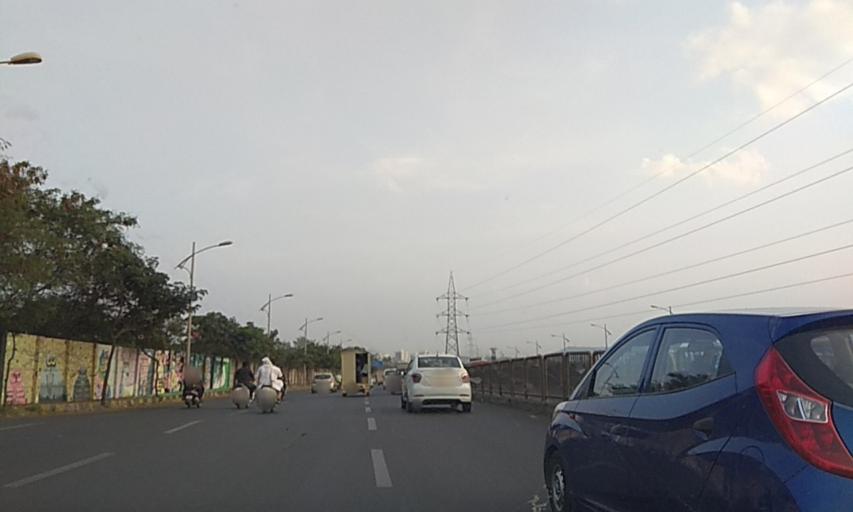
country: IN
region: Maharashtra
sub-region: Pune Division
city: Pimpri
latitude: 18.5792
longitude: 73.8009
